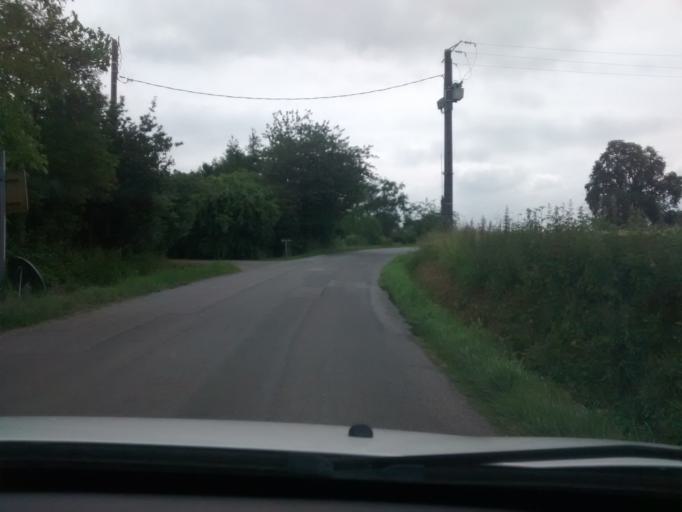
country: FR
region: Brittany
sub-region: Departement d'Ille-et-Vilaine
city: Brece
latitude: 48.1300
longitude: -1.4838
